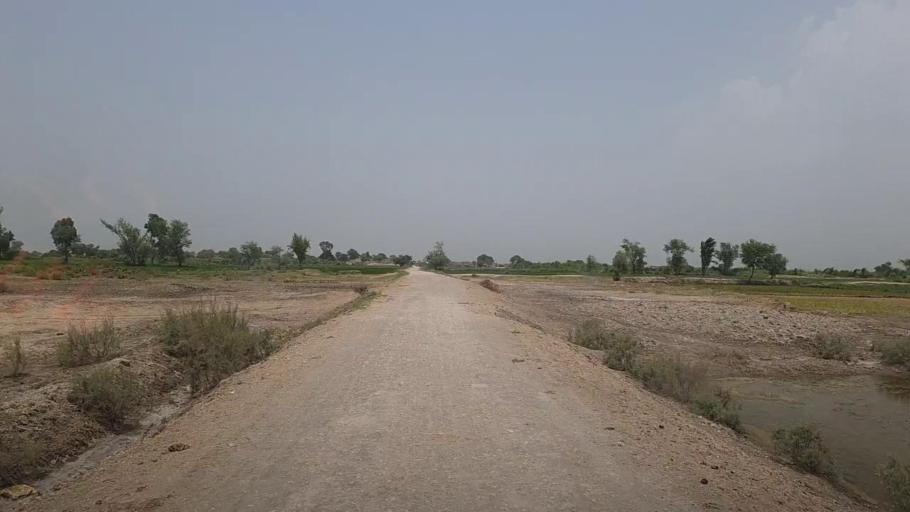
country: PK
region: Sindh
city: Sita Road
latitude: 27.0781
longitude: 67.8715
